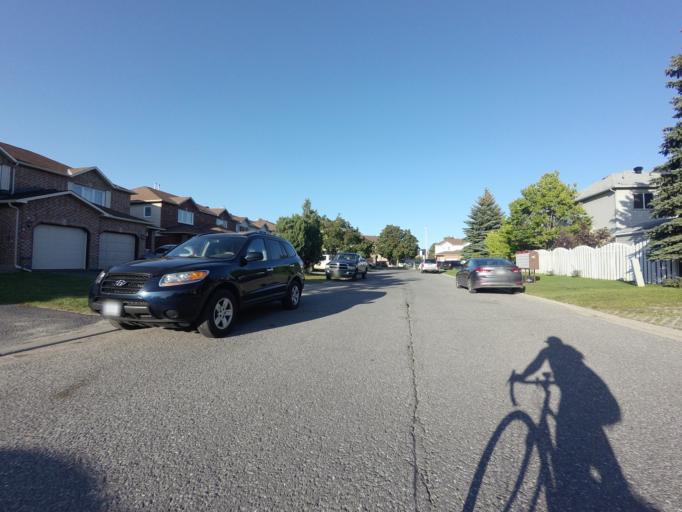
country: CA
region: Ontario
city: Bells Corners
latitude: 45.2833
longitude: -75.7244
